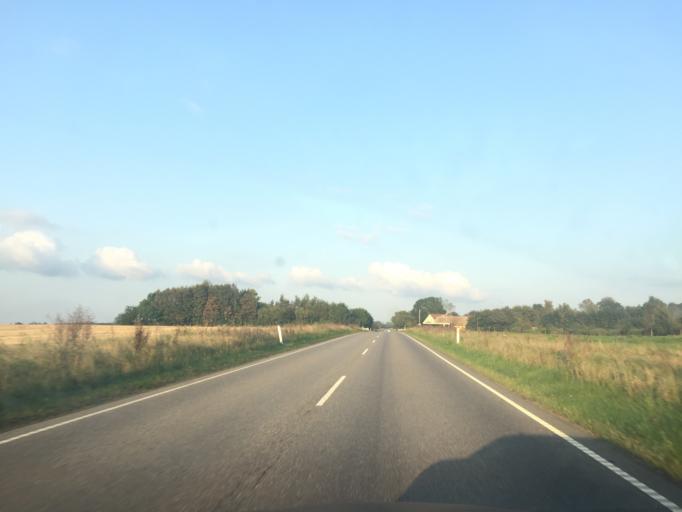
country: DK
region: Zealand
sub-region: Holbaek Kommune
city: Tollose
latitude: 55.5498
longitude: 11.7436
